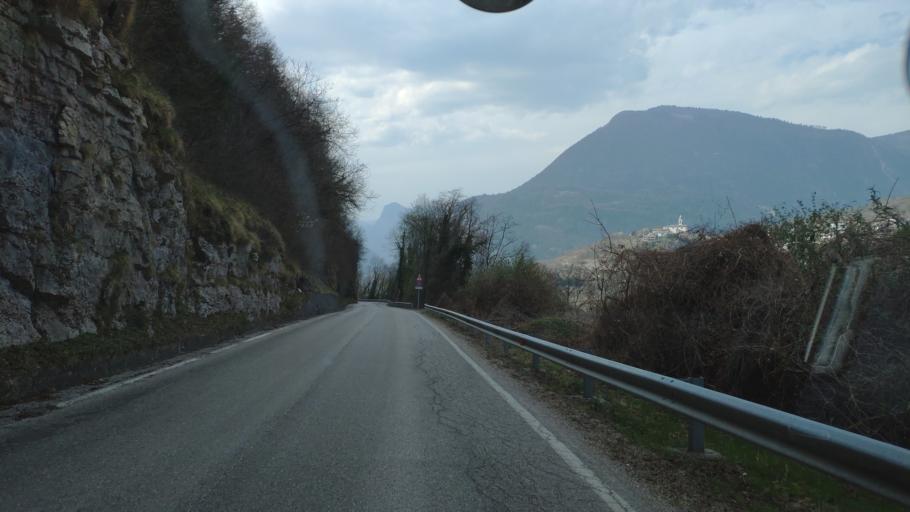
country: IT
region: Veneto
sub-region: Provincia di Vicenza
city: Enego
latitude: 45.9507
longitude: 11.7200
